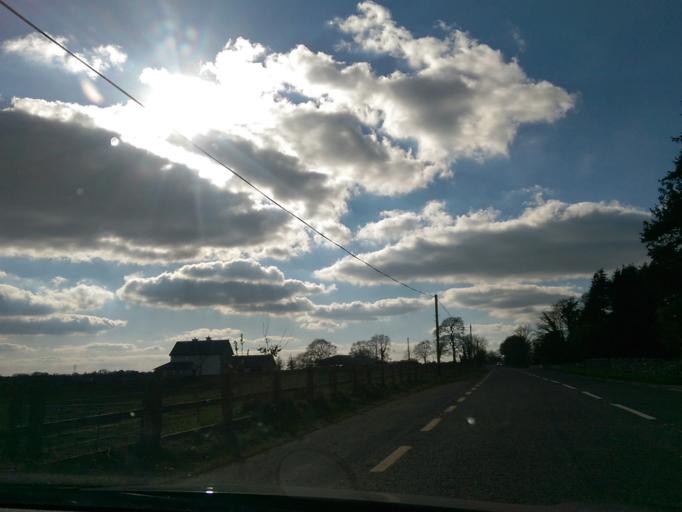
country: IE
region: Connaught
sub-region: County Galway
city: Portumna
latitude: 53.1887
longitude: -8.3693
